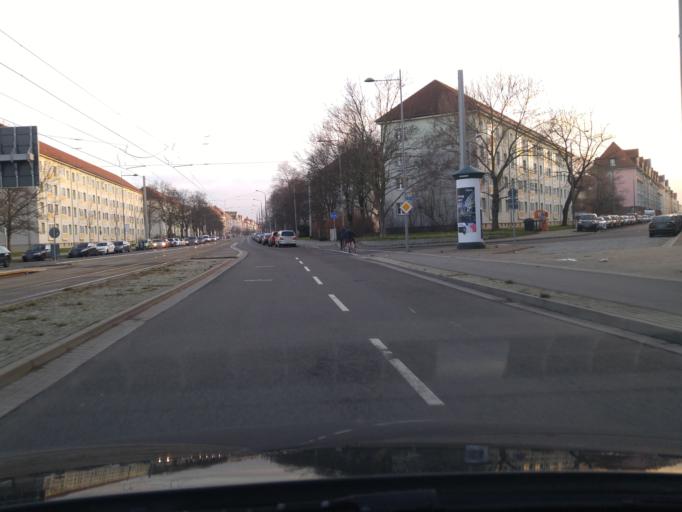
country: DE
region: Saxony
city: Leipzig
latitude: 51.3753
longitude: 12.3614
